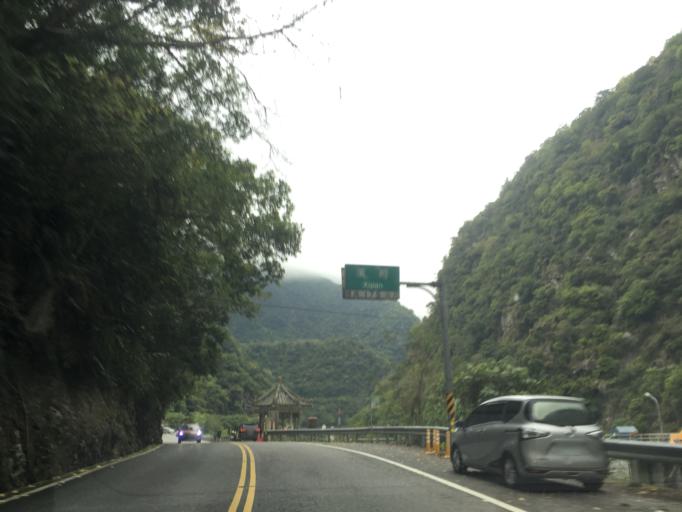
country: TW
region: Taiwan
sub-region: Hualien
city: Hualian
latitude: 24.1768
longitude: 121.5843
